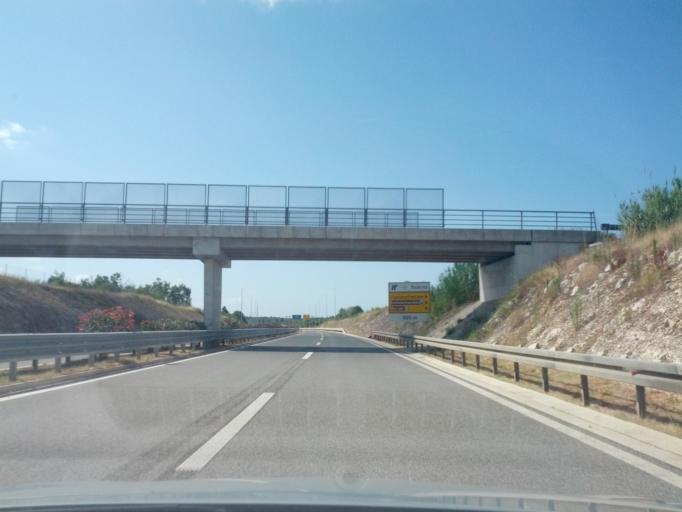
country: HR
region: Istarska
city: Karojba
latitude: 45.2237
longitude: 13.7219
